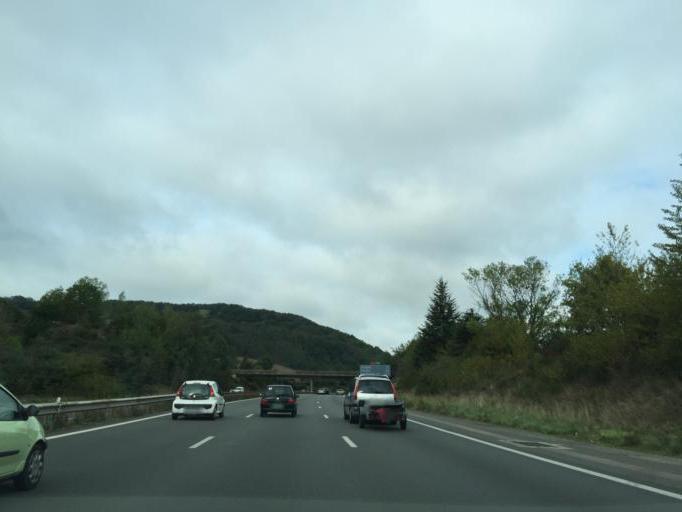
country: FR
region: Rhone-Alpes
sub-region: Departement de la Loire
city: La Fouillouse
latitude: 45.4864
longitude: 4.3270
